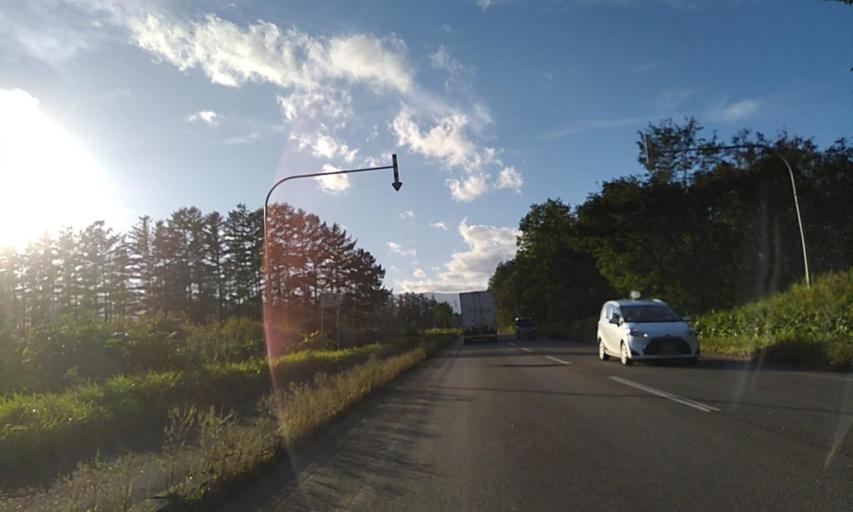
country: JP
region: Hokkaido
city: Otofuke
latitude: 42.9553
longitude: 142.9187
